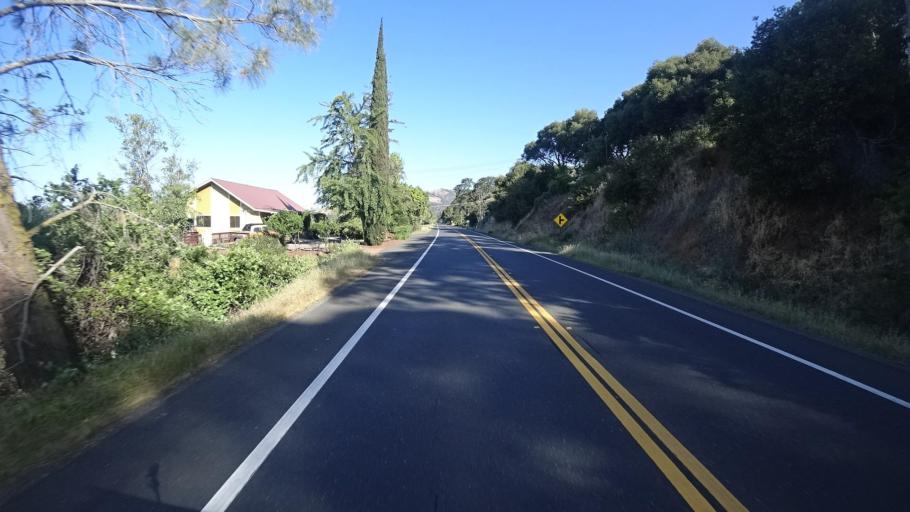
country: US
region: California
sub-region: Lake County
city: Soda Bay
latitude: 39.0284
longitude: -122.7366
